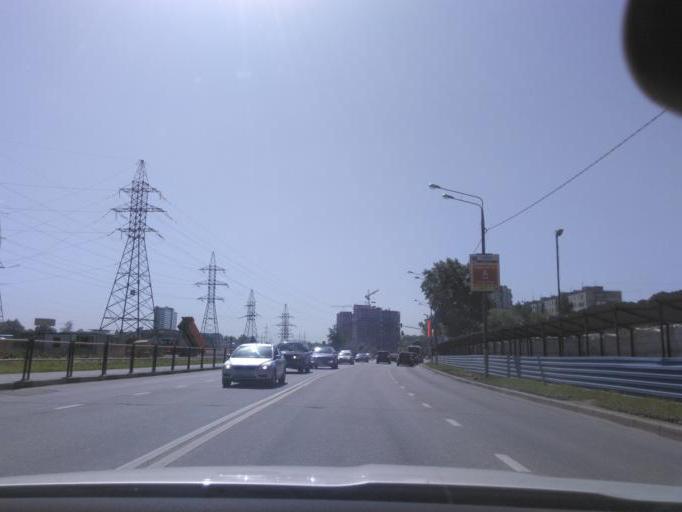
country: RU
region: Moscow
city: Khimki
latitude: 55.9021
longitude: 37.4157
